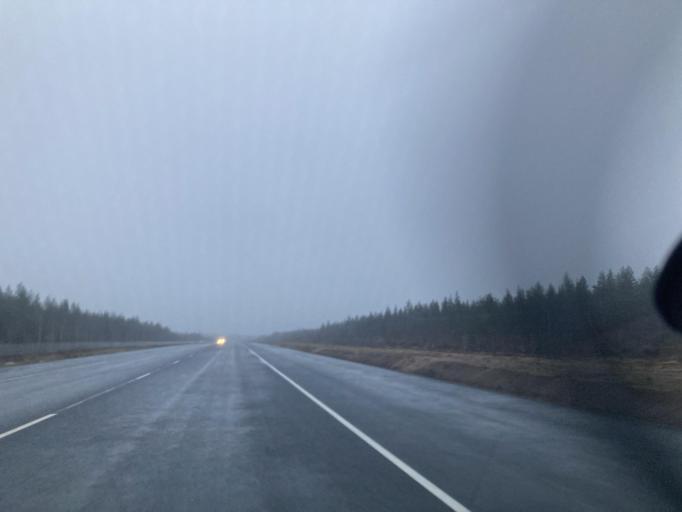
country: FI
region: Lapland
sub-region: Rovaniemi
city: Rovaniemi
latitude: 66.5753
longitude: 25.7985
